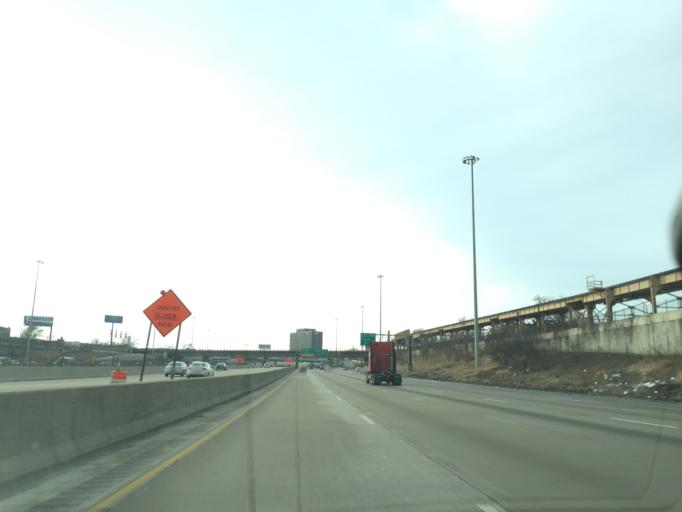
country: US
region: Illinois
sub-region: Cook County
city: Chicago
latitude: 41.7845
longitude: -87.6314
